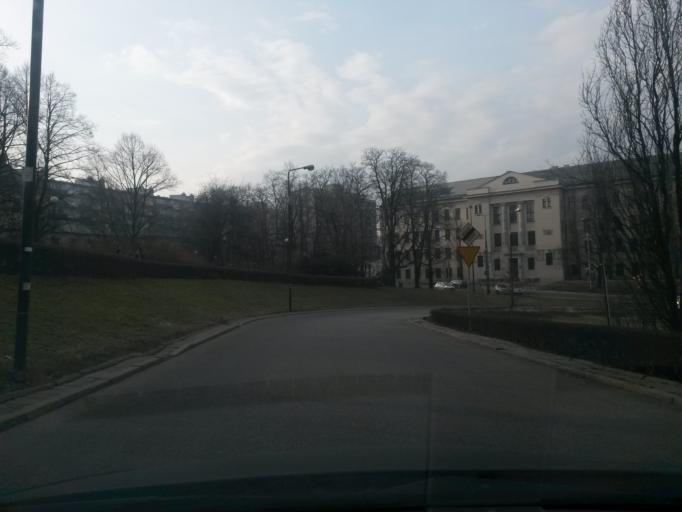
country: PL
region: Masovian Voivodeship
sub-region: Warszawa
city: Warsaw
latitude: 52.2457
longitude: 21.0092
